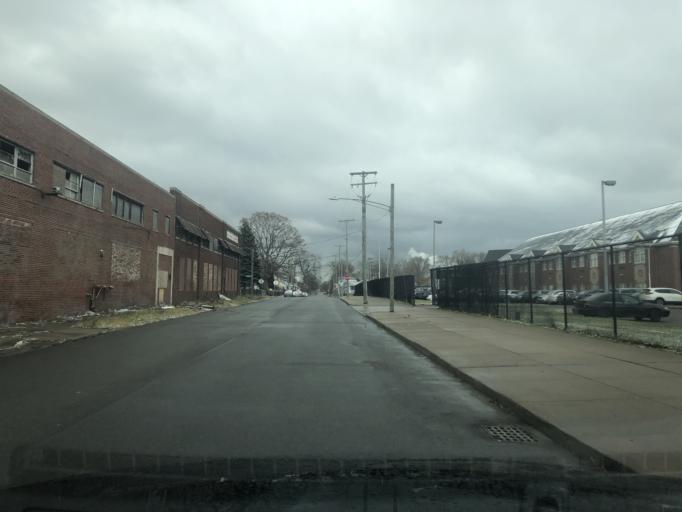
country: US
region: Michigan
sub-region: Wayne County
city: River Rouge
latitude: 42.3106
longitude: -83.1159
